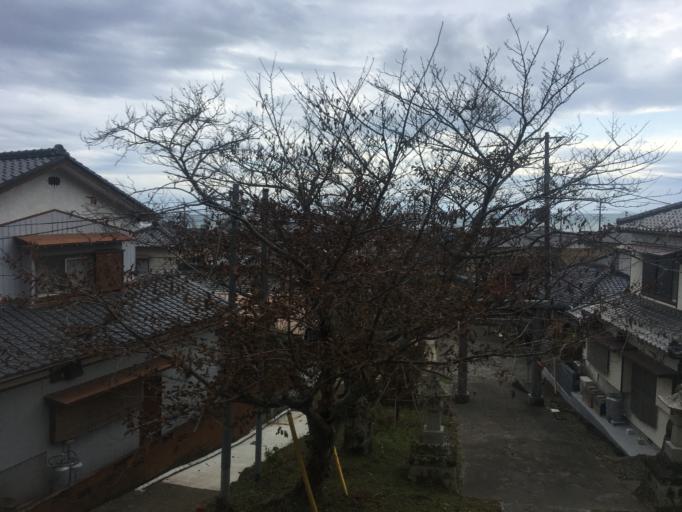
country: JP
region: Chiba
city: Kawaguchi
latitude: 35.0378
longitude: 140.0107
